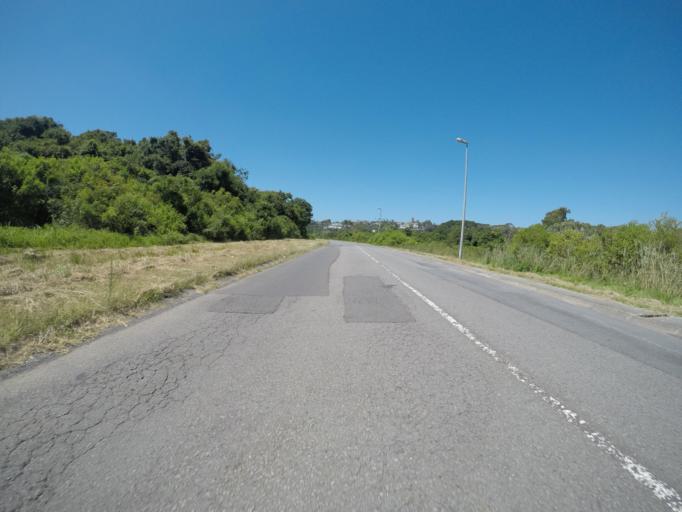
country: ZA
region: Eastern Cape
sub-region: Buffalo City Metropolitan Municipality
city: East London
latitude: -32.9770
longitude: 27.9333
